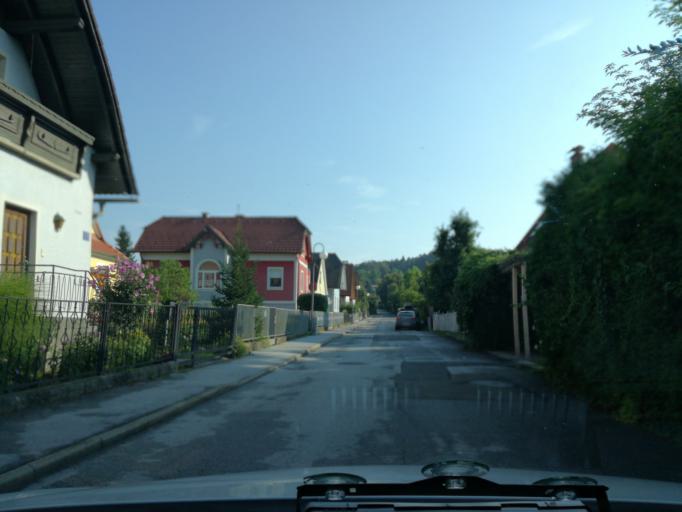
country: AT
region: Styria
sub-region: Politischer Bezirk Weiz
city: Gleisdorf
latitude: 47.1098
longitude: 15.7121
